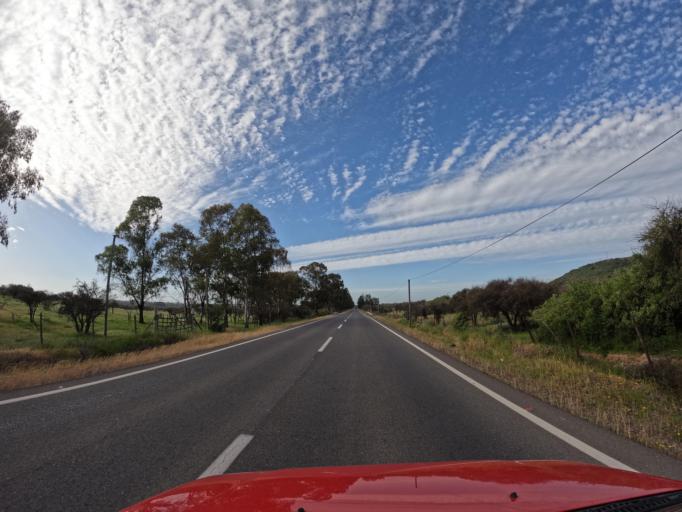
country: CL
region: O'Higgins
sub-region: Provincia de Colchagua
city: Santa Cruz
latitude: -34.1788
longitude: -71.7325
